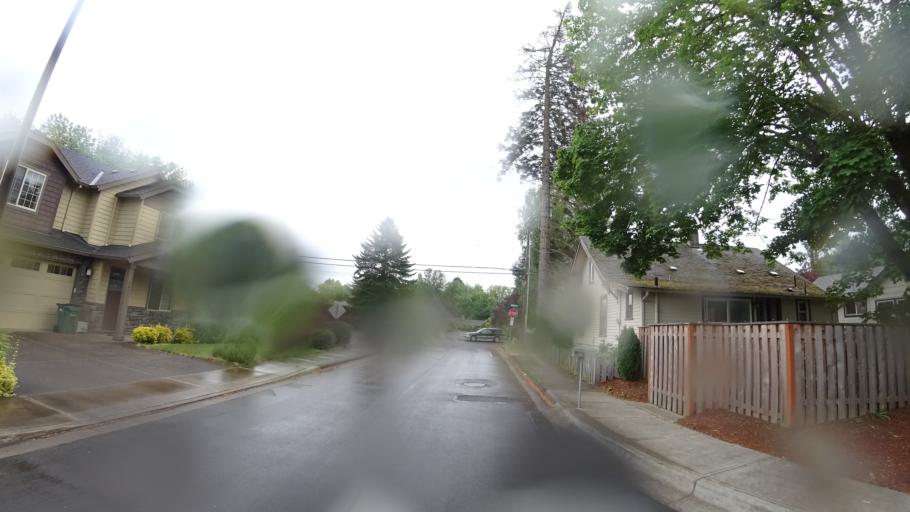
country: US
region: Oregon
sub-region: Washington County
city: Garden Home-Whitford
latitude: 45.4679
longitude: -122.7715
